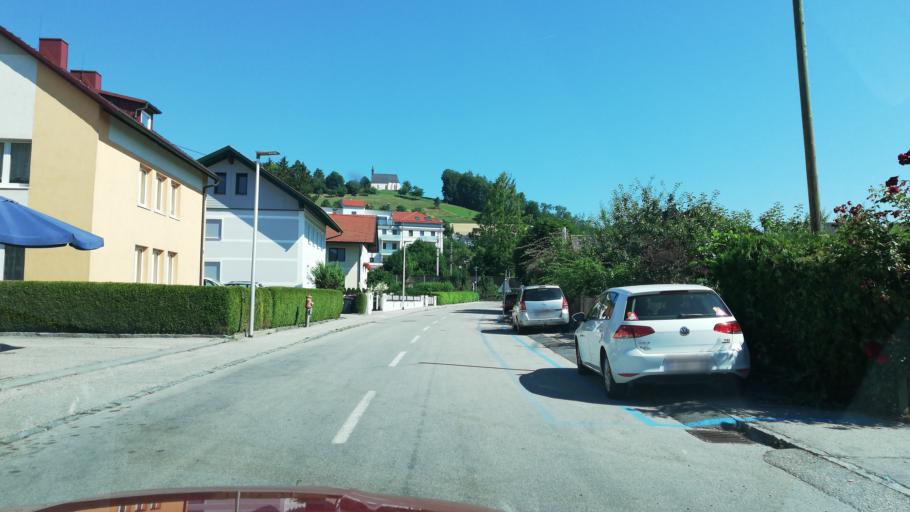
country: AT
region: Upper Austria
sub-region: Politischer Bezirk Grieskirchen
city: Bad Schallerbach
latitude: 48.2285
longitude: 13.9147
